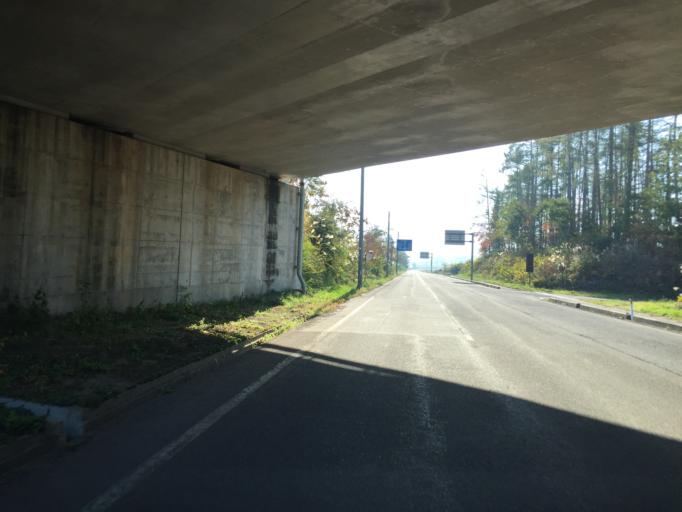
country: JP
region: Fukushima
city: Kitakata
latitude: 37.7202
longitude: 139.8700
